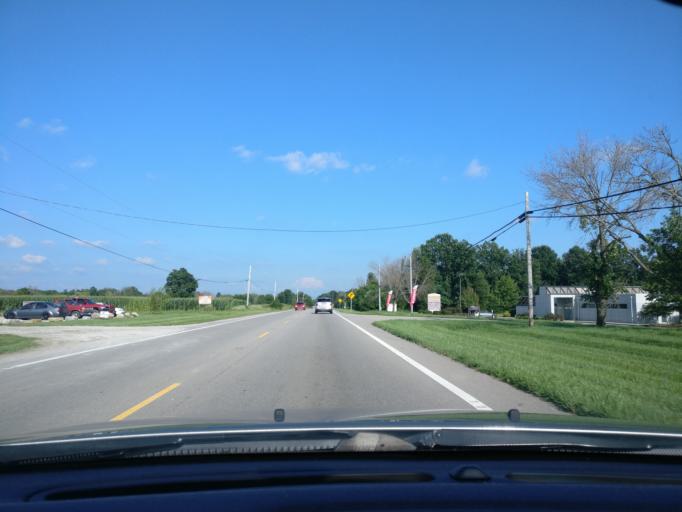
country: US
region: Ohio
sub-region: Warren County
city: Waynesville
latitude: 39.5426
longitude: -84.1101
